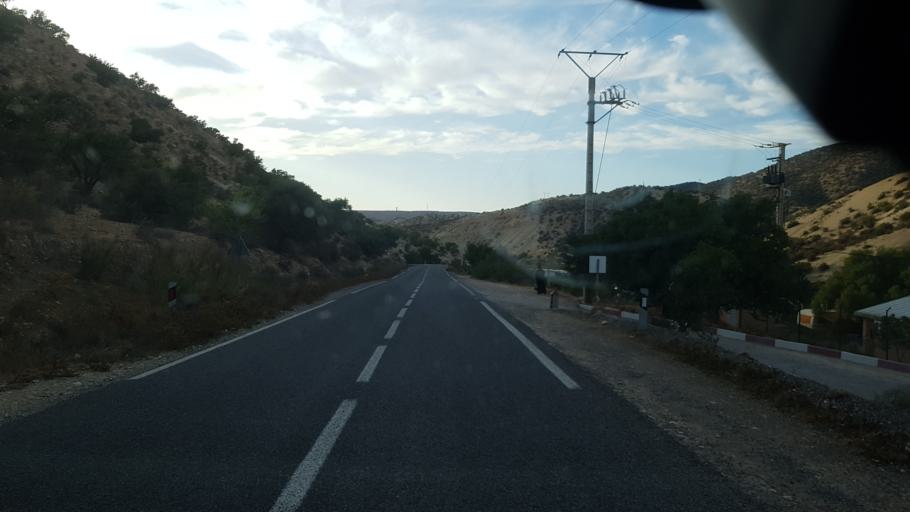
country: MA
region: Souss-Massa-Draa
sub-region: Agadir-Ida-ou-Tnan
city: Aourir
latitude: 30.4945
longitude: -9.6234
